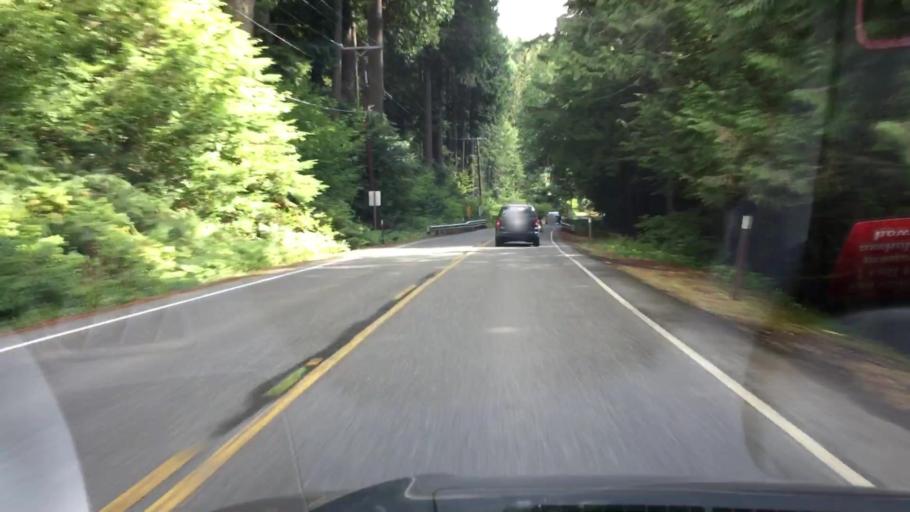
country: US
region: Washington
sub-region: Pierce County
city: Eatonville
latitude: 46.7478
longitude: -121.9254
